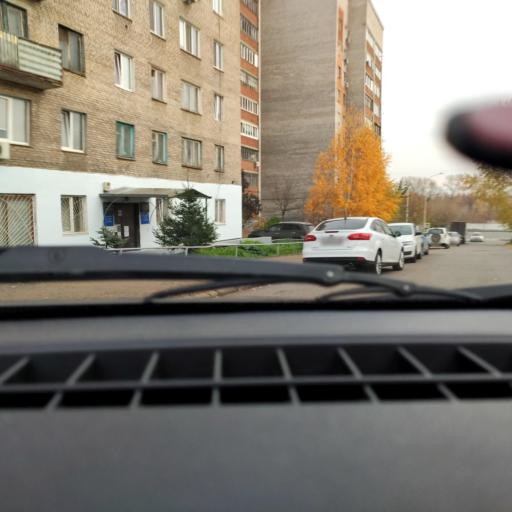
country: RU
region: Bashkortostan
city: Ufa
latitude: 54.8023
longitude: 56.1327
